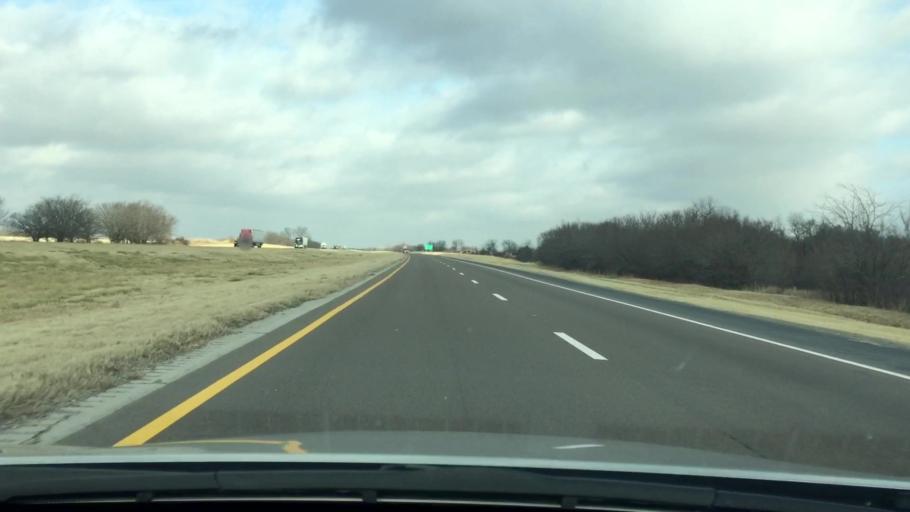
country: US
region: Oklahoma
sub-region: Garvin County
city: Maysville
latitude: 34.8343
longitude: -97.3122
